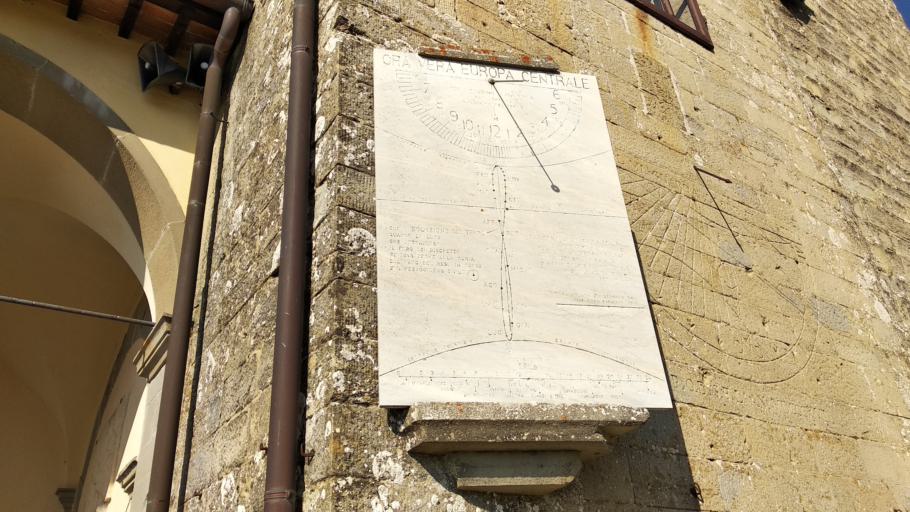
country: IT
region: Tuscany
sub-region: Province of Arezzo
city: Chiusi della Verna
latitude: 43.7071
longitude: 11.9306
